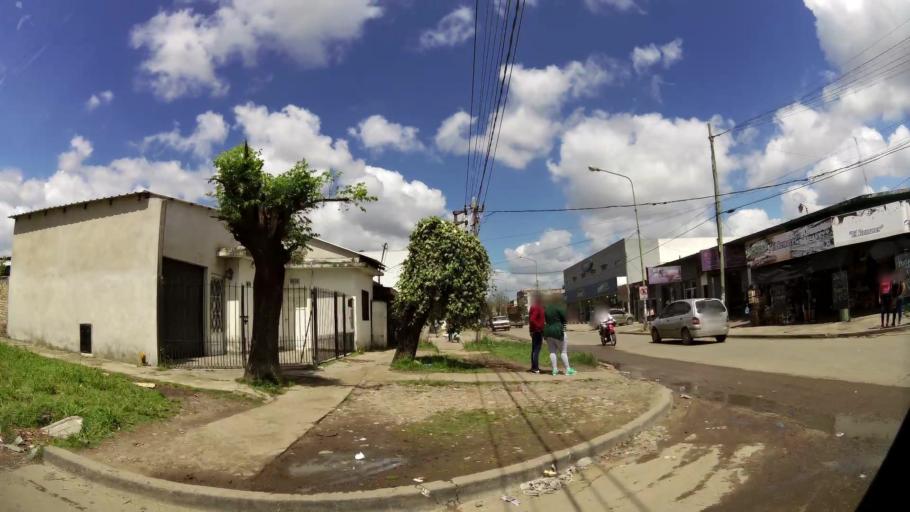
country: AR
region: Buenos Aires
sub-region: Partido de Quilmes
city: Quilmes
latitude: -34.8274
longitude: -58.2268
